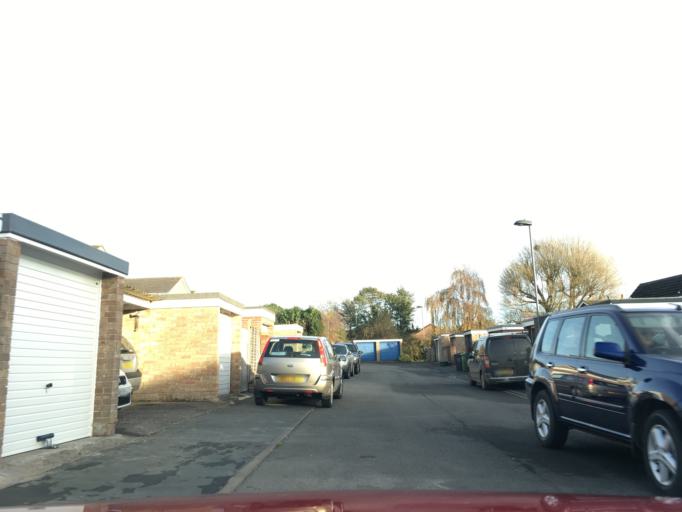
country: GB
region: England
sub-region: South Gloucestershire
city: Thornbury
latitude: 51.6177
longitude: -2.5162
